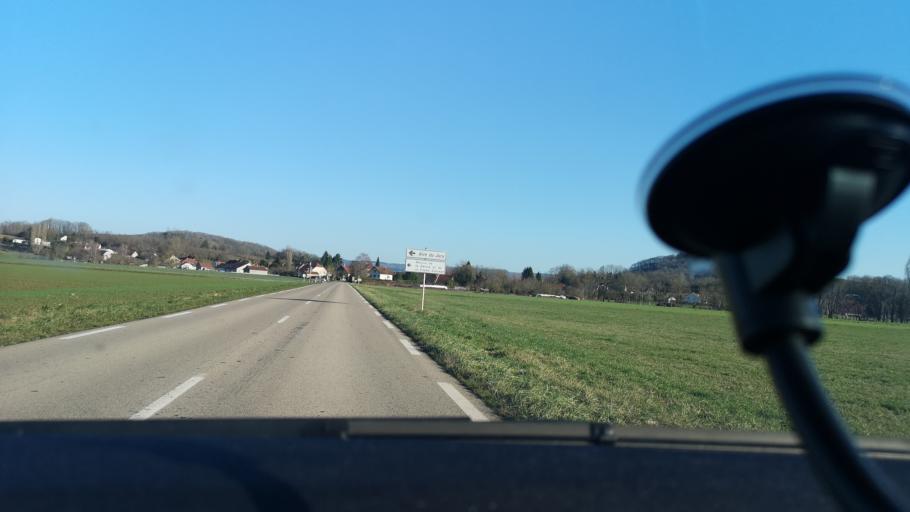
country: FR
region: Franche-Comte
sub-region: Departement du Jura
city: Bletterans
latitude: 46.7601
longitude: 5.5153
